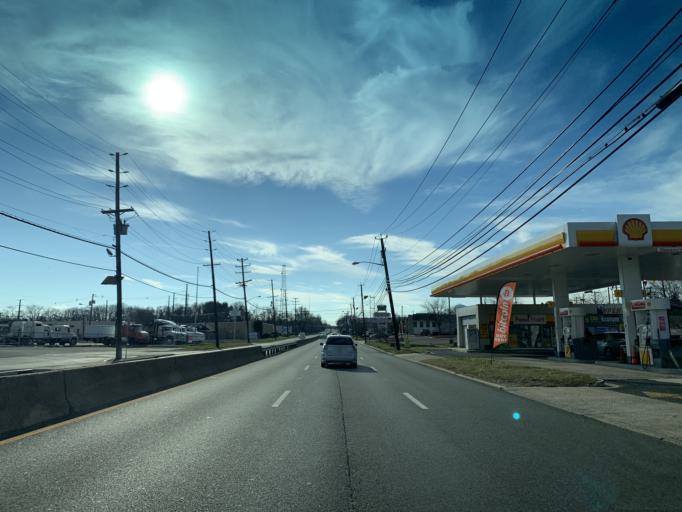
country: US
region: New Jersey
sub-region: Camden County
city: Pennsauken
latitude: 39.9707
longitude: -75.0432
